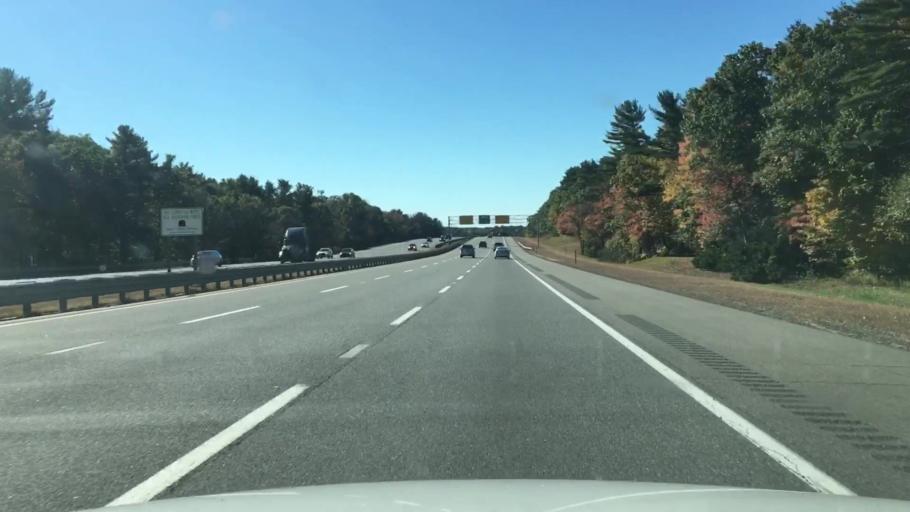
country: US
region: Maine
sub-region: York County
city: York Harbor
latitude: 43.1726
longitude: -70.6516
